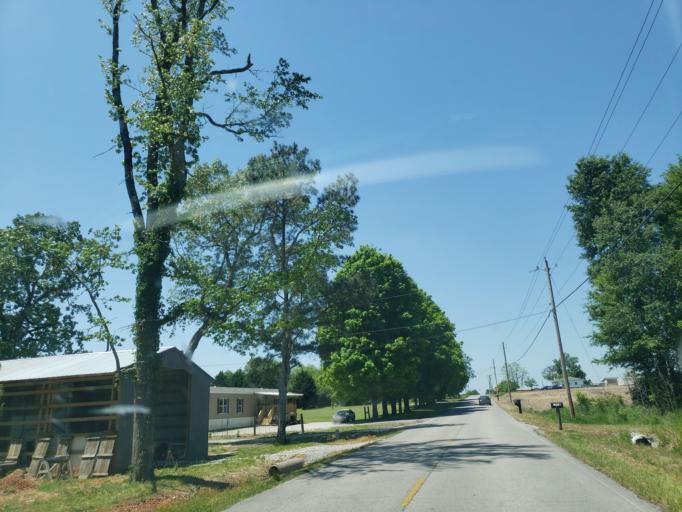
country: US
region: Alabama
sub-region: Madison County
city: Harvest
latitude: 34.9625
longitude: -86.7214
